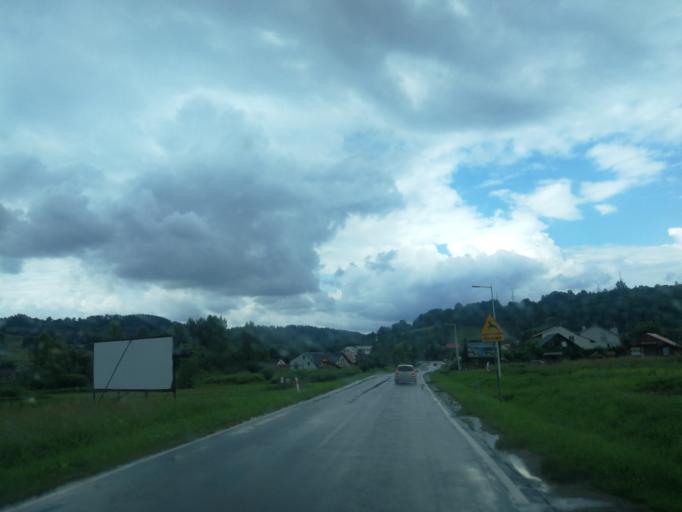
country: PL
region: Subcarpathian Voivodeship
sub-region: Powiat leski
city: Polanczyk
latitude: 49.4117
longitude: 22.4483
